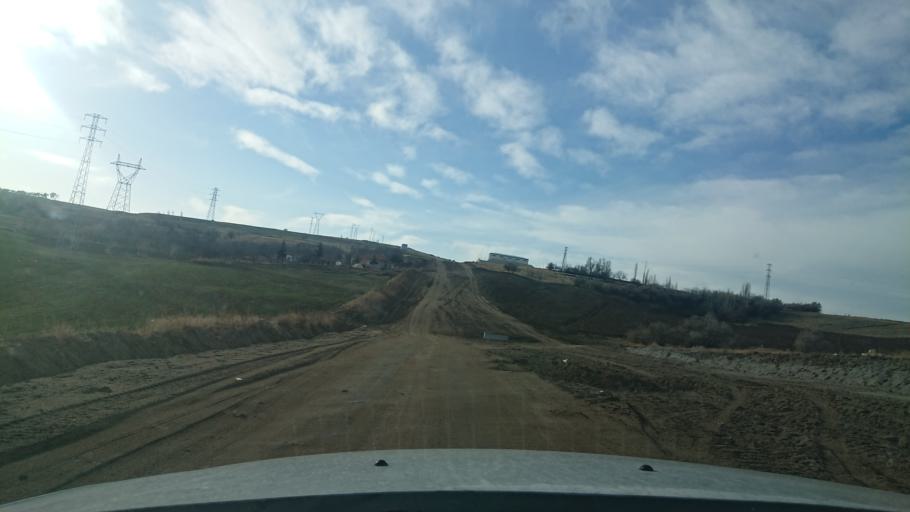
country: TR
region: Aksaray
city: Agacoren
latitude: 38.8575
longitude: 33.9429
